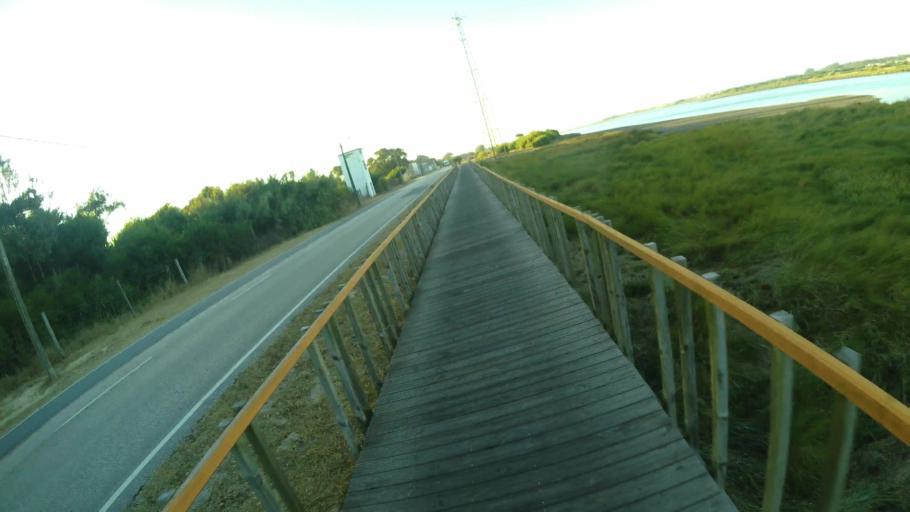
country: PT
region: Aveiro
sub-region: Ilhavo
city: Gafanha da Encarnacao
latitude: 40.5682
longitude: -8.7567
